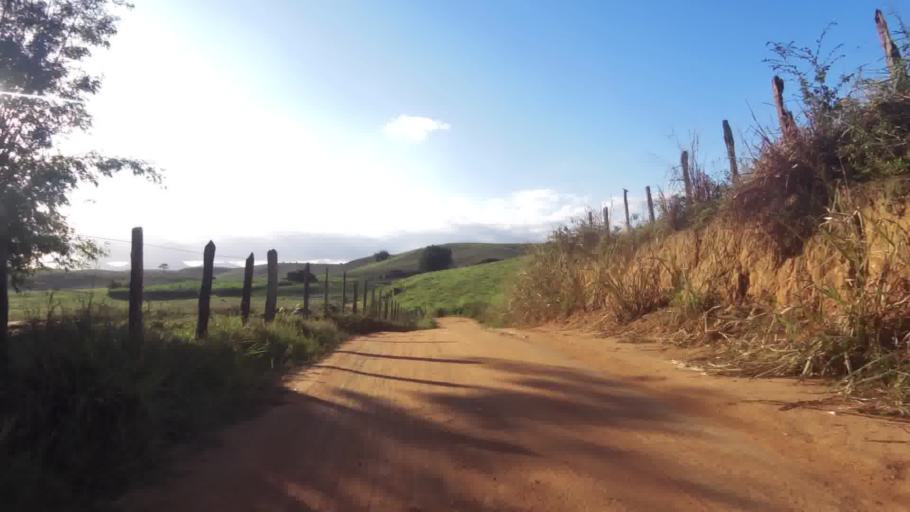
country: BR
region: Espirito Santo
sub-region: Marataizes
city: Marataizes
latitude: -21.1343
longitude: -41.0185
